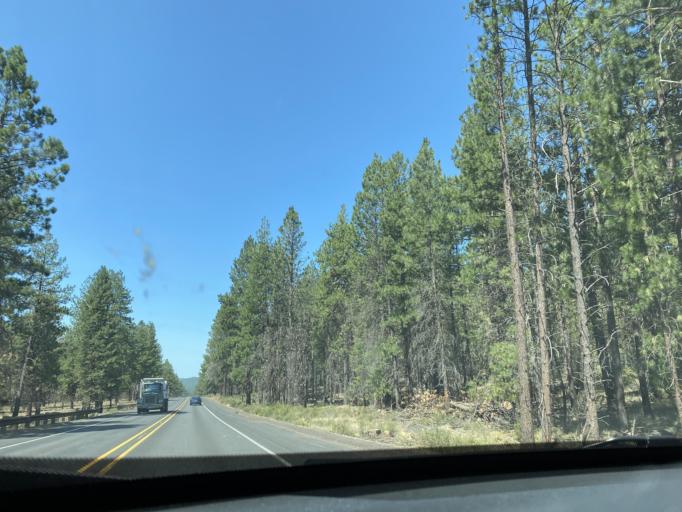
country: US
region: Oregon
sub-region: Deschutes County
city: Sunriver
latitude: 43.8694
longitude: -121.4151
